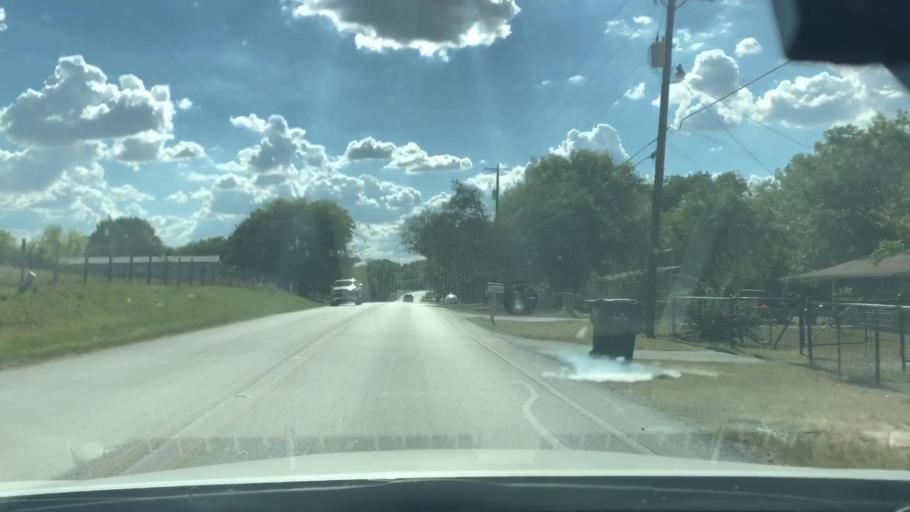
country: US
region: Texas
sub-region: Guadalupe County
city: Northcliff
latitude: 29.6628
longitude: -98.1816
